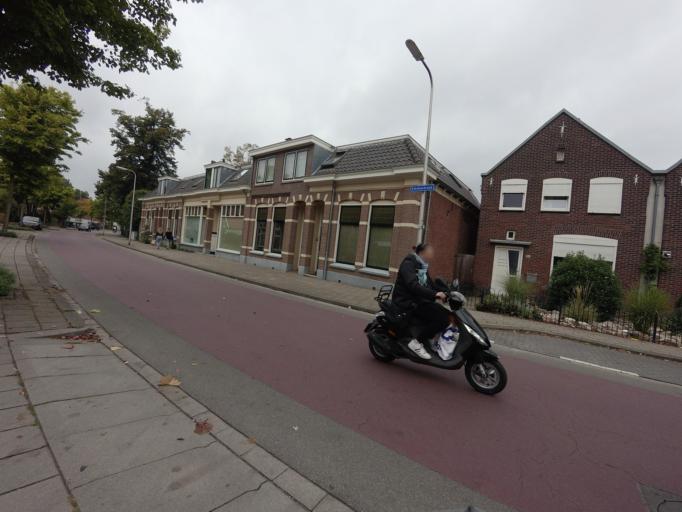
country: NL
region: Overijssel
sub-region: Gemeente Enschede
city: Enschede
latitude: 52.2171
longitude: 6.8852
